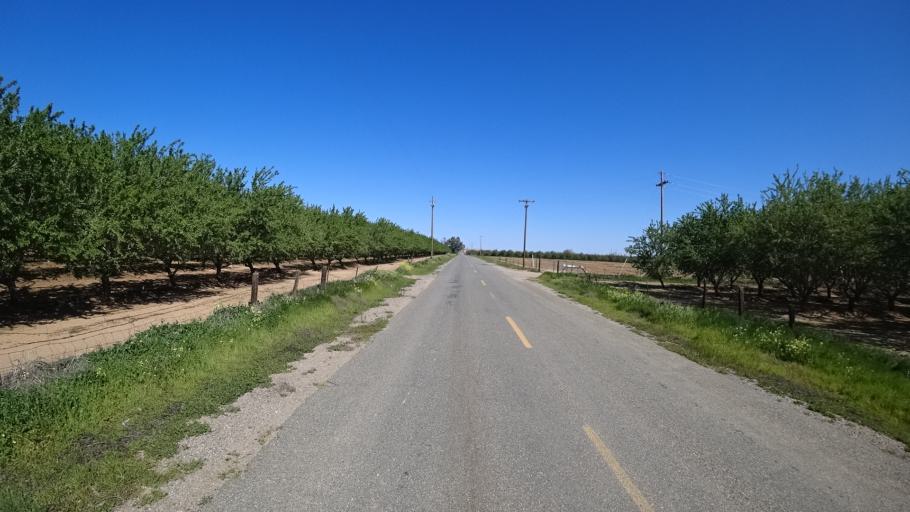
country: US
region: California
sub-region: Glenn County
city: Orland
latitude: 39.6865
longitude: -122.2716
